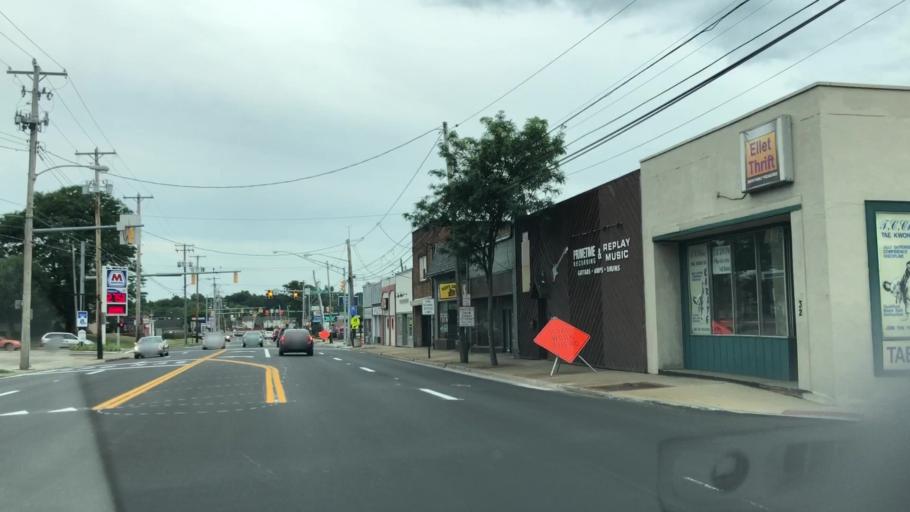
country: US
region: Ohio
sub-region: Summit County
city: Sawyerwood
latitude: 41.0465
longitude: -81.4372
